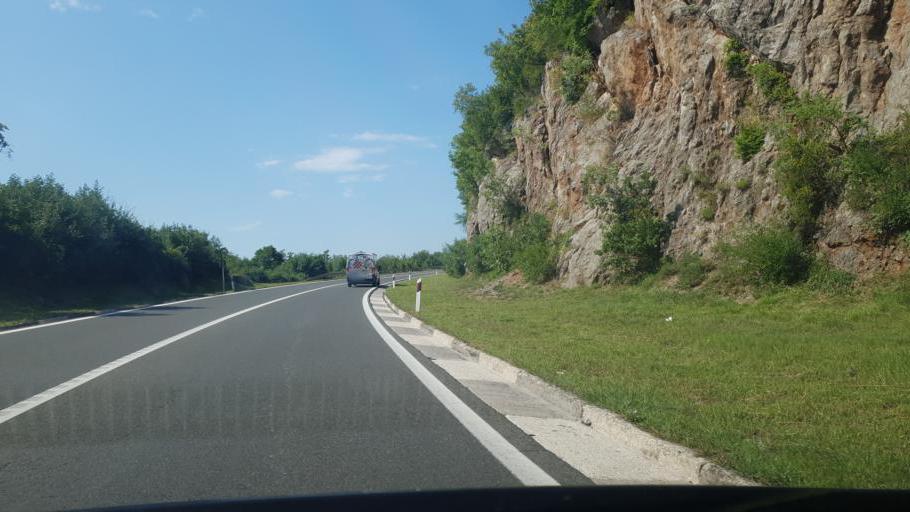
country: HR
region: Primorsko-Goranska
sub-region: Grad Opatija
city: Opatija
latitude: 45.3490
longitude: 14.3065
